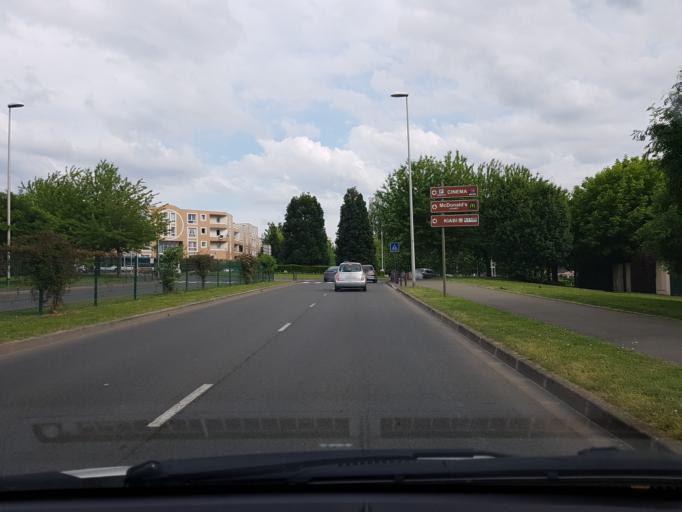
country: FR
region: Ile-de-France
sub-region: Departement de Seine-et-Marne
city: Torcy
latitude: 48.8432
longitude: 2.6511
